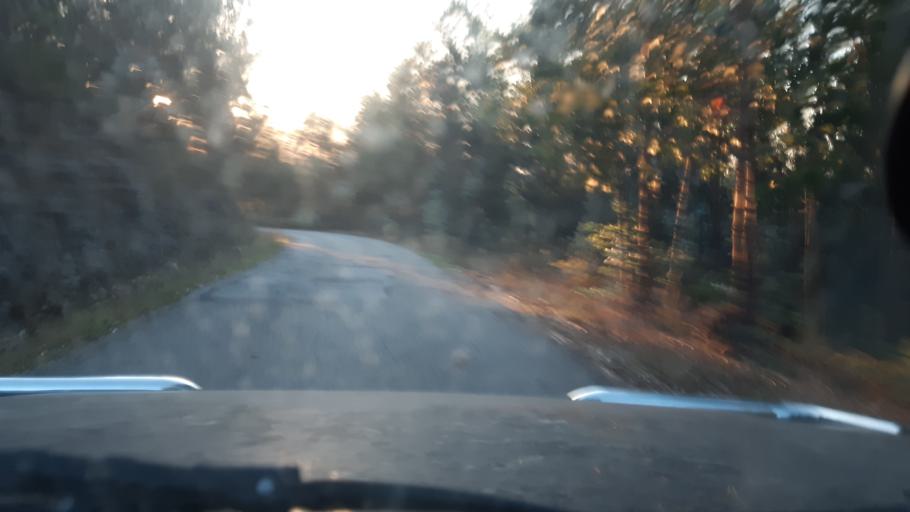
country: PT
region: Aveiro
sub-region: Agueda
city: Aguada de Cima
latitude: 40.5635
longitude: -8.3485
